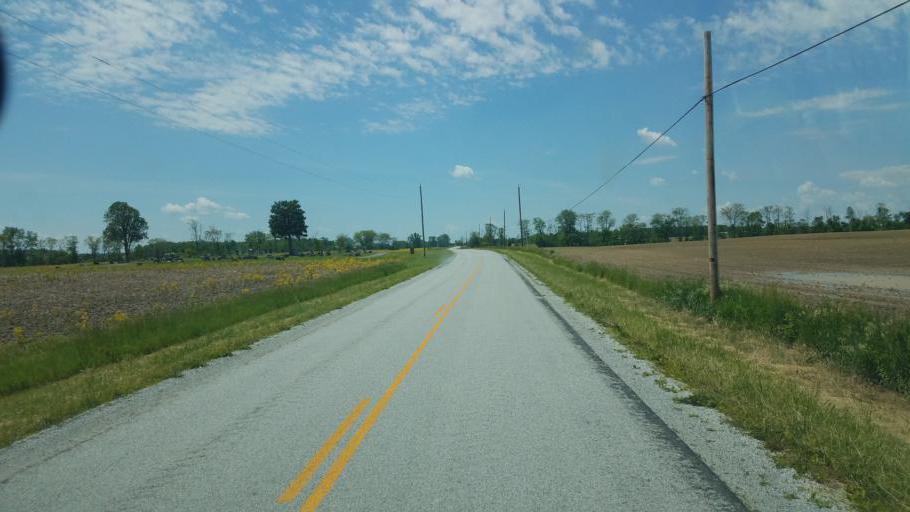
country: US
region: Ohio
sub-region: Hardin County
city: Forest
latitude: 40.6649
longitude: -83.4517
